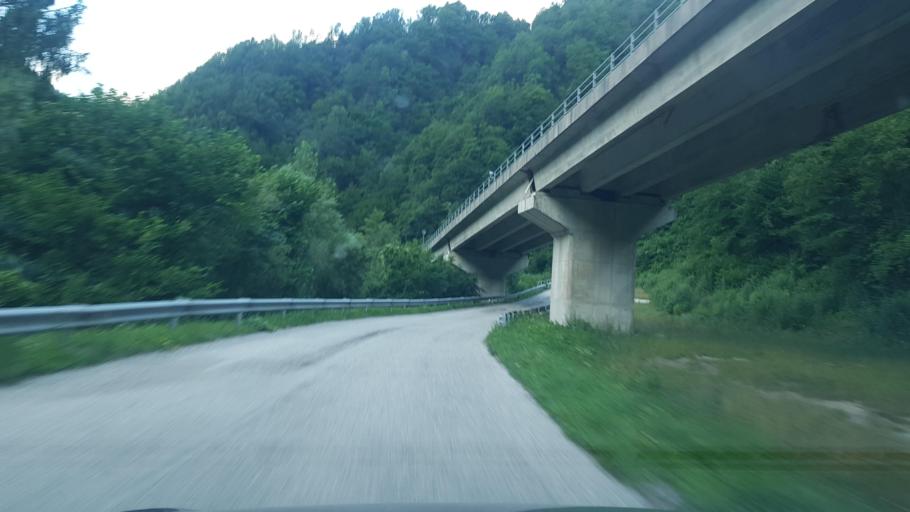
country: IT
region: Friuli Venezia Giulia
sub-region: Provincia di Udine
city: Paularo
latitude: 46.4810
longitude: 13.0895
